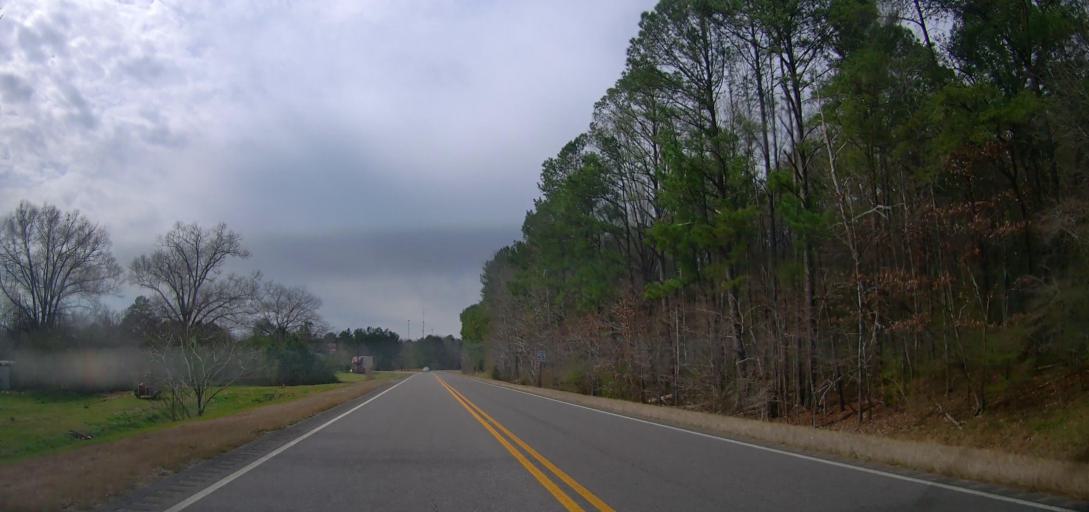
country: US
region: Alabama
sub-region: Walker County
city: Carbon Hill
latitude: 33.9010
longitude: -87.5450
